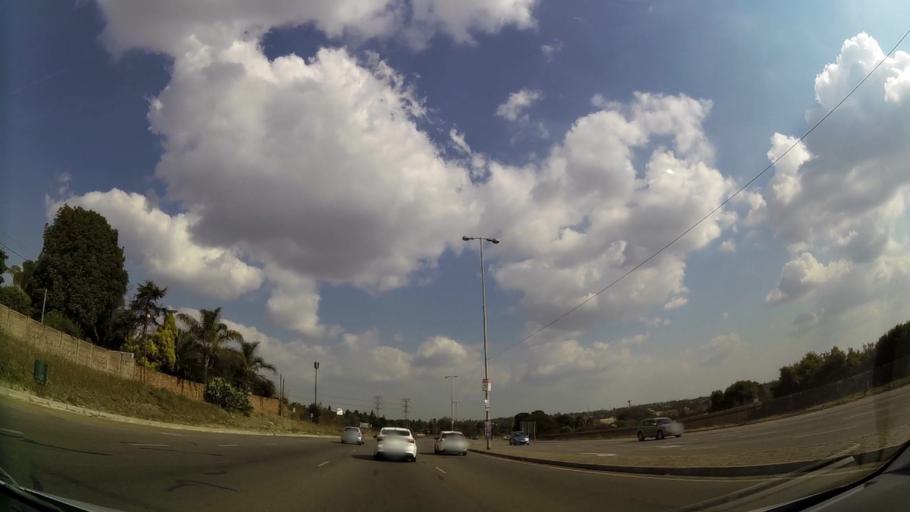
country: ZA
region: Gauteng
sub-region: City of Tshwane Metropolitan Municipality
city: Centurion
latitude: -25.8200
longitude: 28.2715
